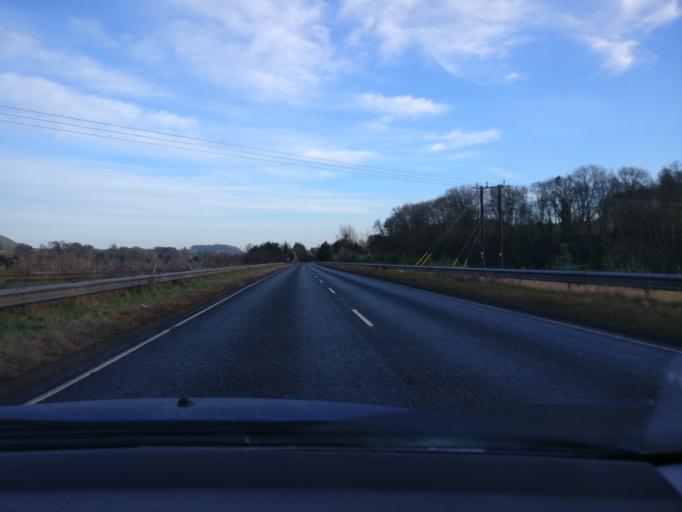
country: GB
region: Scotland
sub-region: The Scottish Borders
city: Hawick
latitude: 55.4494
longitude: -2.7236
